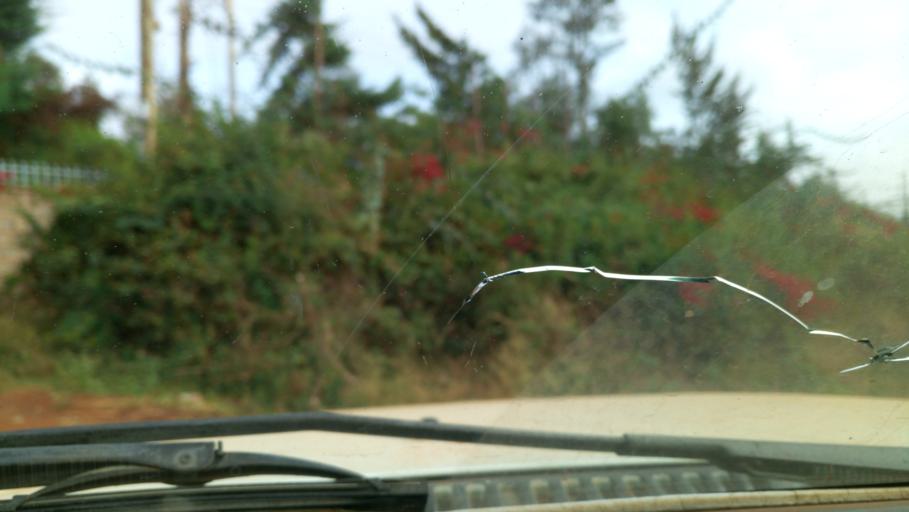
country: KE
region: Murang'a District
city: Maragua
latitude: -0.8537
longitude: 37.1413
